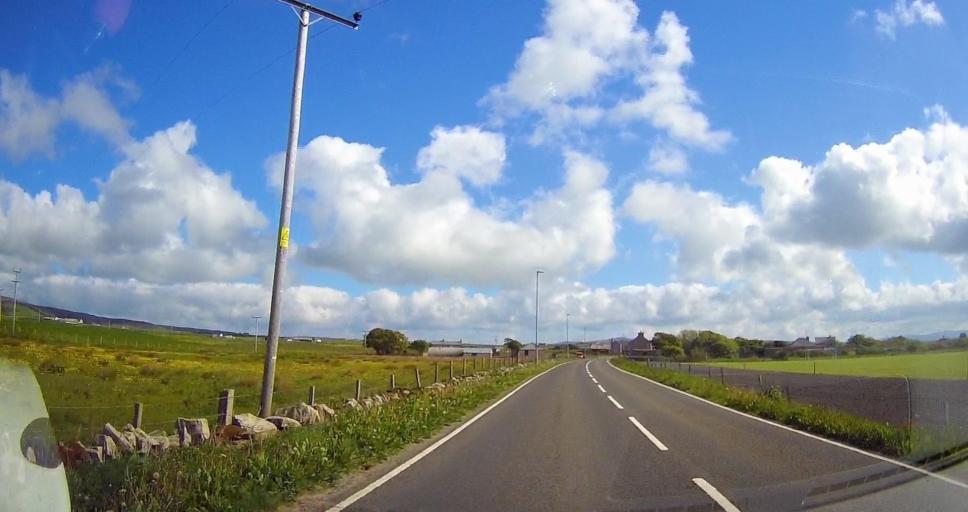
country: GB
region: Scotland
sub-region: Orkney Islands
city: Stromness
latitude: 59.0391
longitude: -3.1877
